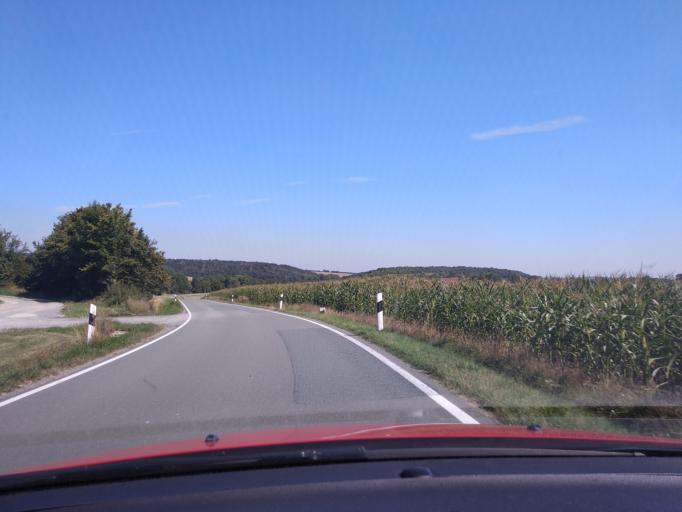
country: DE
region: North Rhine-Westphalia
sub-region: Regierungsbezirk Detmold
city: Willebadessen
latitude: 51.6557
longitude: 9.0638
